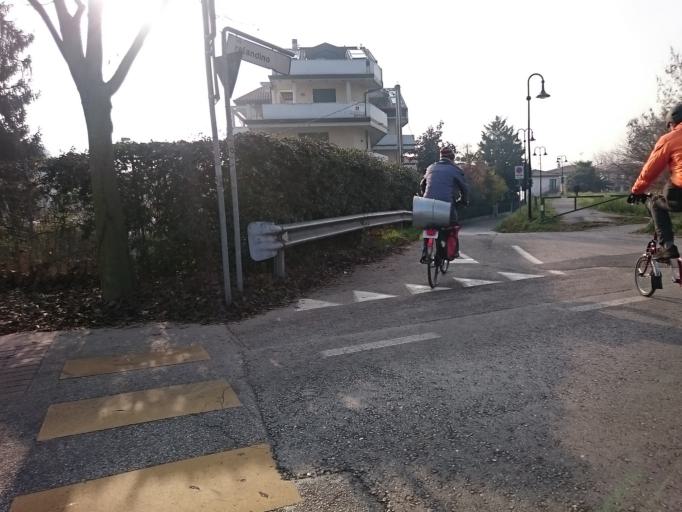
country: IT
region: Veneto
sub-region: Provincia di Padova
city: Padova
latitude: 45.4080
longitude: 11.9005
